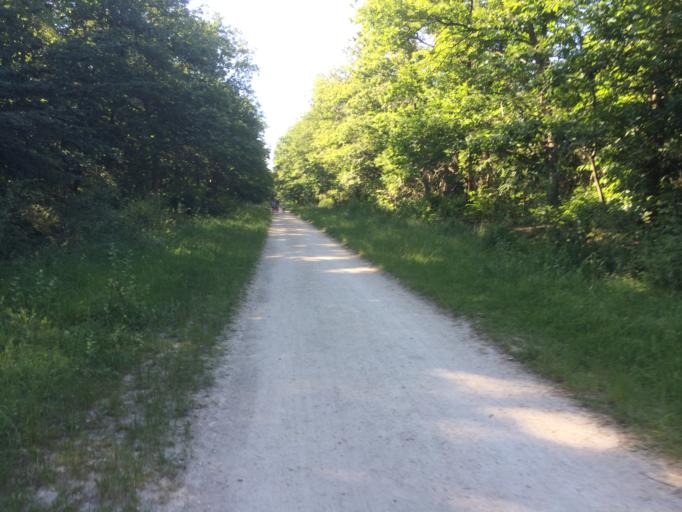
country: FR
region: Ile-de-France
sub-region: Departement du Val-de-Marne
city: Sucy-en-Brie
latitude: 48.7505
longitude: 2.5507
